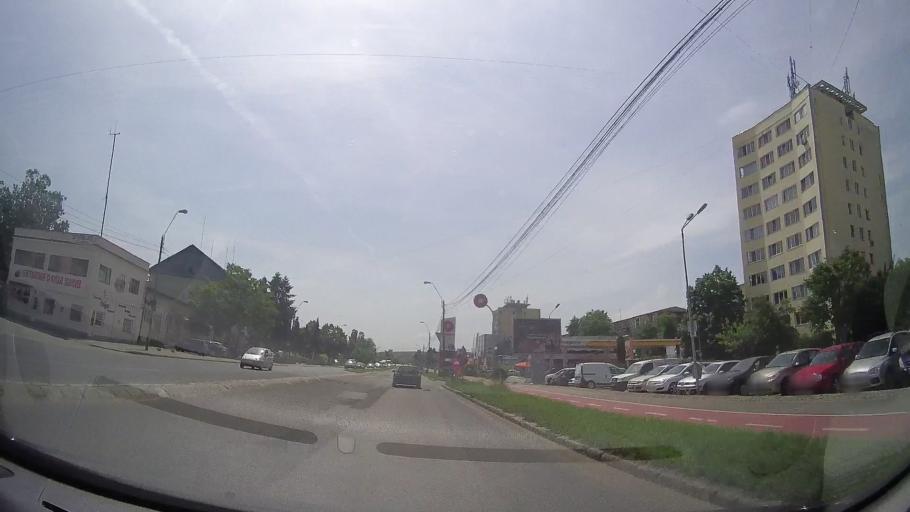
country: RO
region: Hunedoara
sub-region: Municipiul Deva
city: Deva
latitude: 45.8770
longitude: 22.9150
